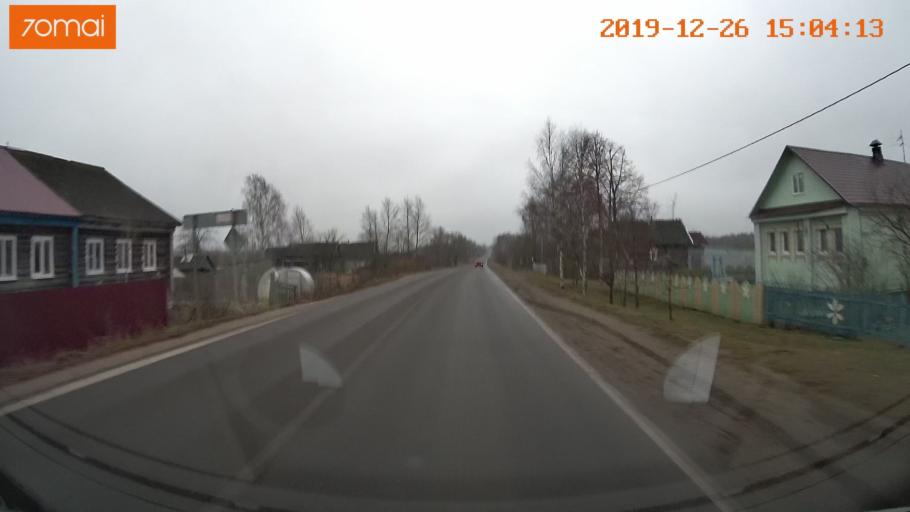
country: RU
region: Jaroslavl
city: Rybinsk
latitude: 58.2025
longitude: 38.8643
